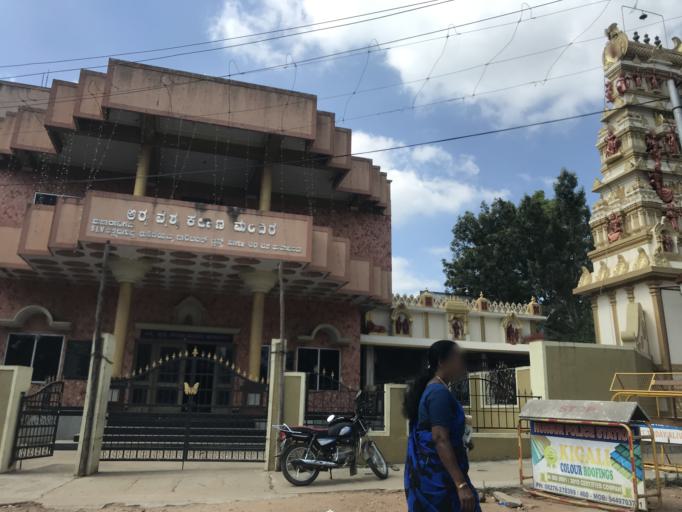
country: IN
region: Karnataka
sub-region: Mysore
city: Hunsur
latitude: 12.3049
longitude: 76.2907
